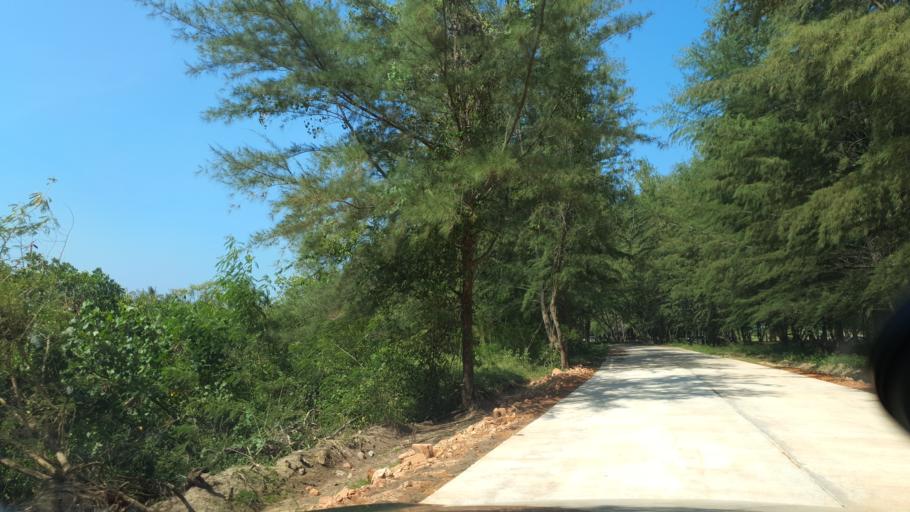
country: TH
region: Surat Thani
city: Tha Chana
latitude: 9.5977
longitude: 99.2095
